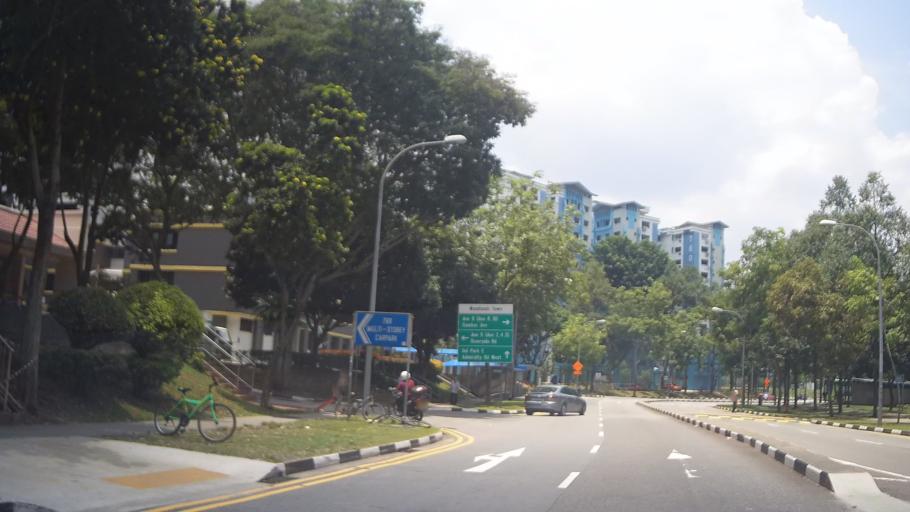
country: MY
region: Johor
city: Johor Bahru
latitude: 1.4463
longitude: 103.7983
